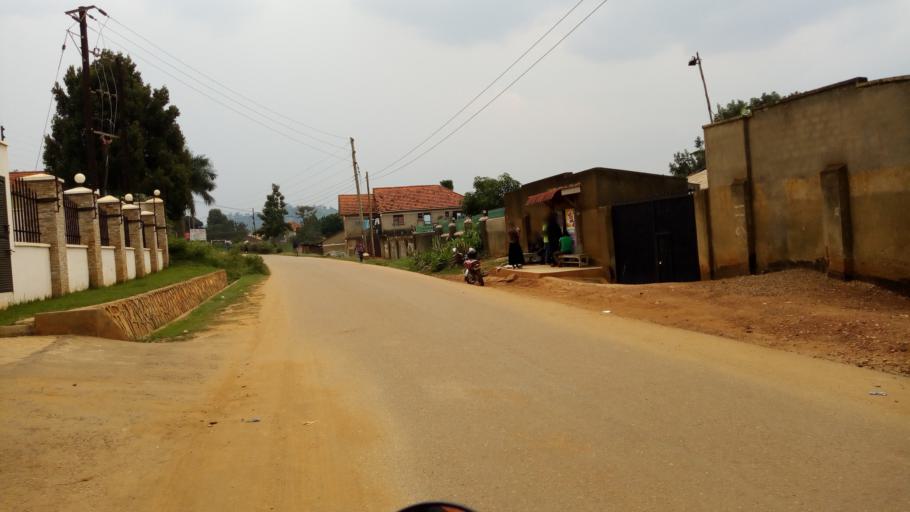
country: UG
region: Central Region
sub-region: Wakiso District
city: Kireka
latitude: 0.3183
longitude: 32.6445
